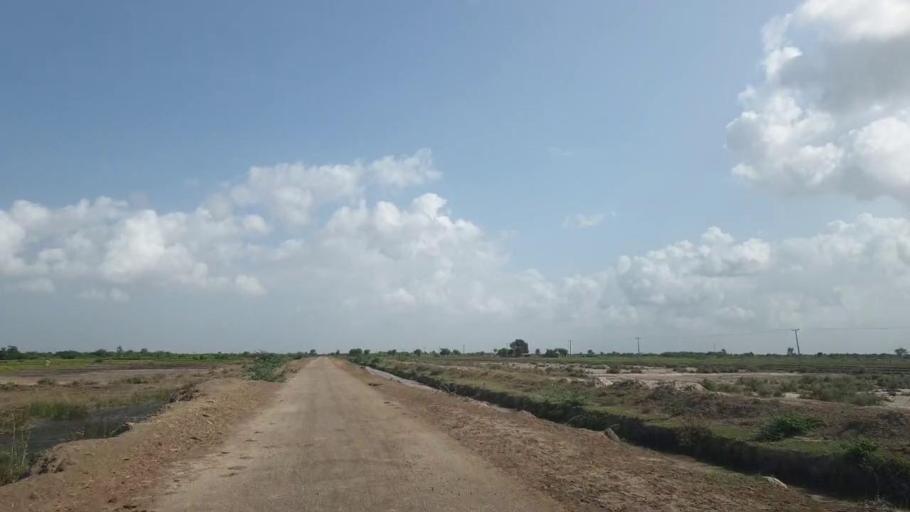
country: PK
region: Sindh
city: Kadhan
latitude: 24.5695
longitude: 69.0674
